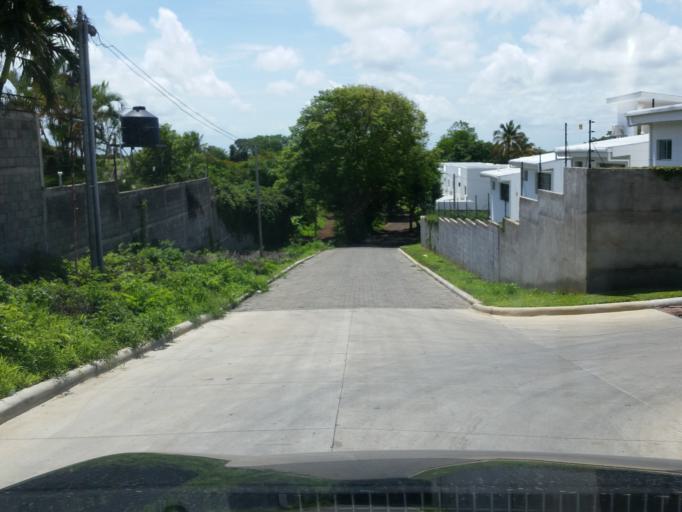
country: NI
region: Managua
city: Managua
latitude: 12.0814
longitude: -86.2389
